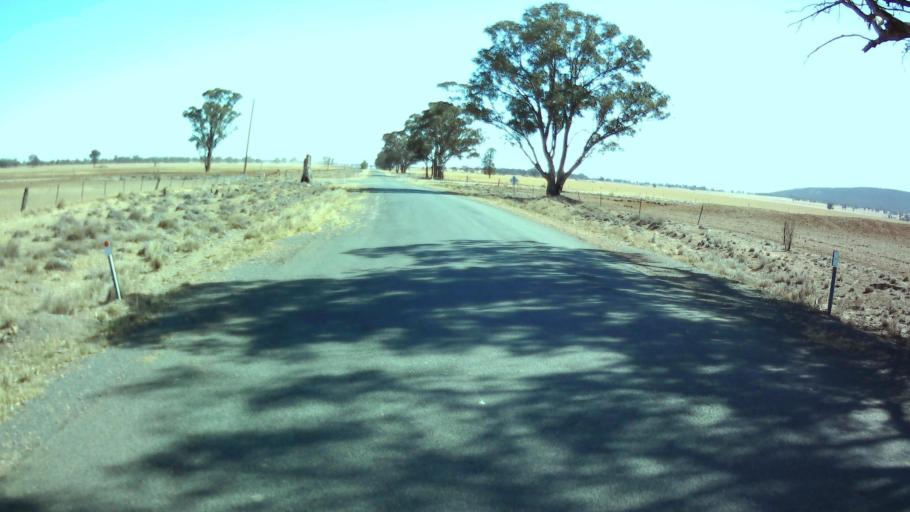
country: AU
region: New South Wales
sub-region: Weddin
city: Grenfell
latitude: -33.7045
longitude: 147.9184
